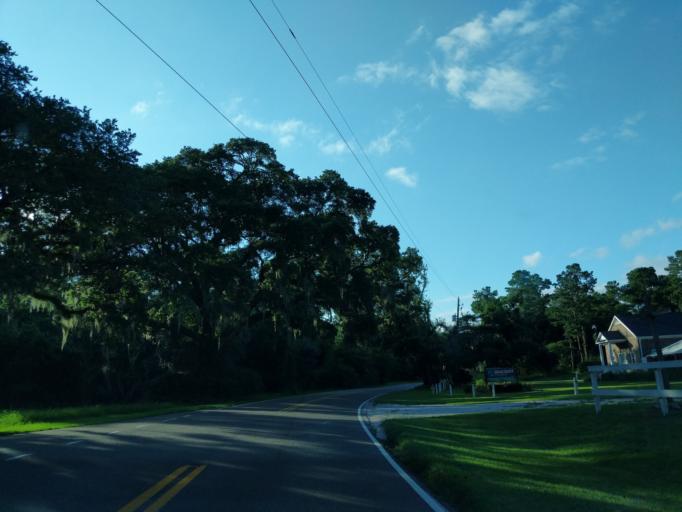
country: US
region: South Carolina
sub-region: Charleston County
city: Awendaw
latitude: 33.0927
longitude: -79.4748
